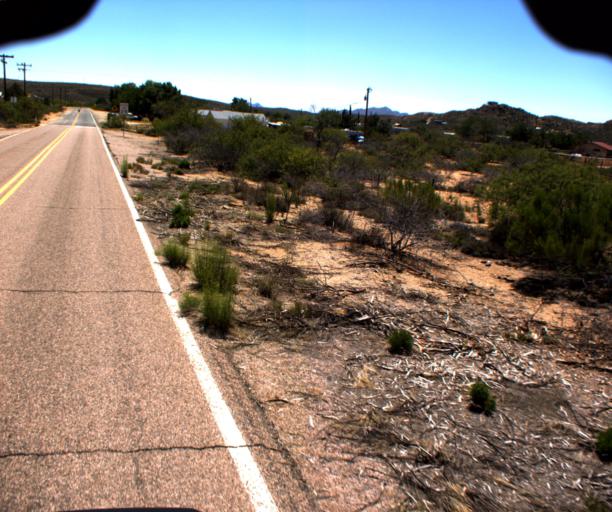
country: US
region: Arizona
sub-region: Yavapai County
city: Congress
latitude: 34.4239
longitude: -112.9161
